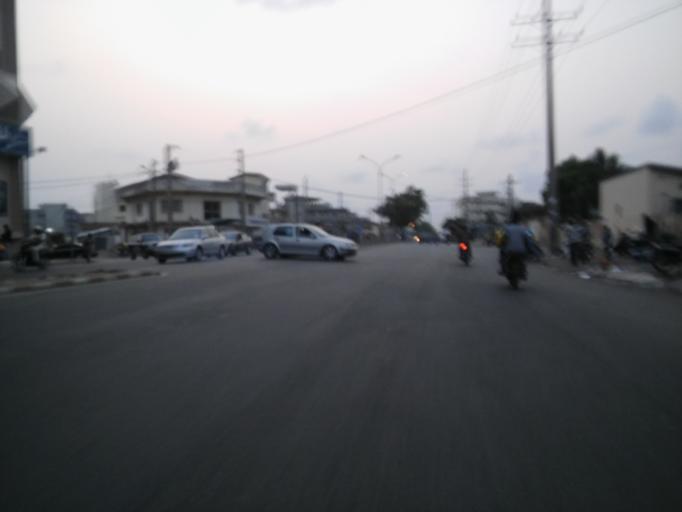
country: BJ
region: Littoral
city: Cotonou
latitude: 6.3711
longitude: 2.4152
